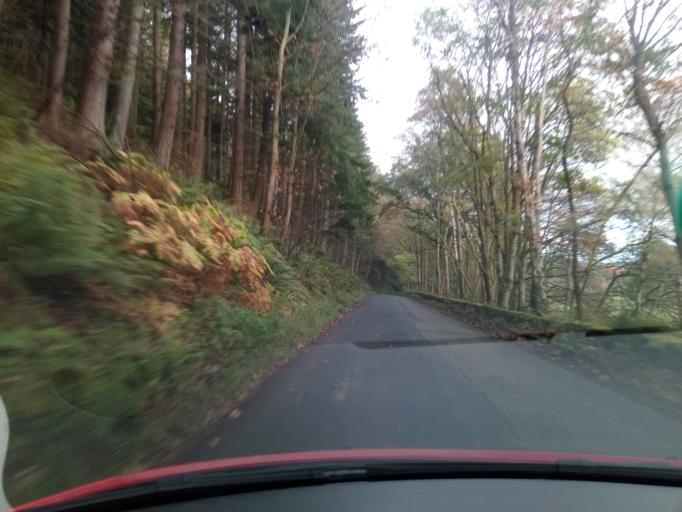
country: GB
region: Scotland
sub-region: The Scottish Borders
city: Innerleithen
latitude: 55.6231
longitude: -3.0970
